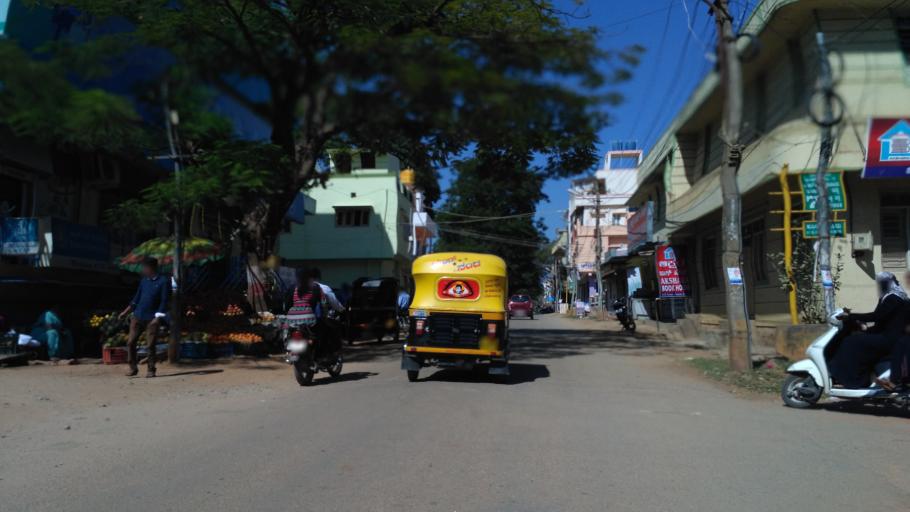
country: IN
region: Karnataka
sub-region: Hassan
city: Hassan
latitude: 13.0082
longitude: 76.1062
